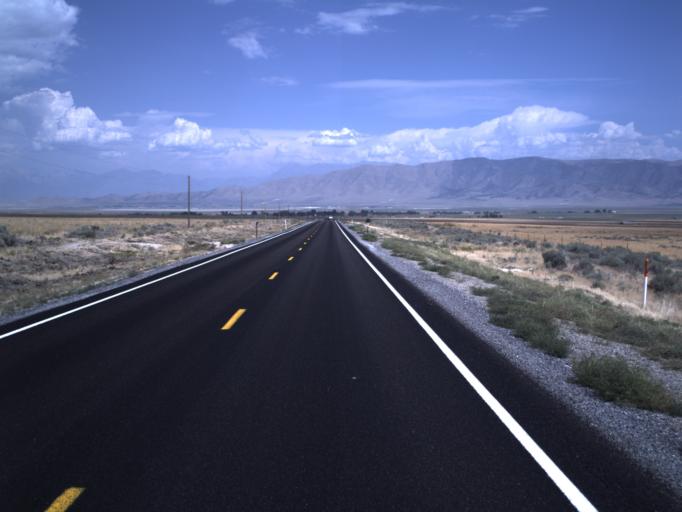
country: US
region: Utah
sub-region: Utah County
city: Eagle Mountain
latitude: 40.2454
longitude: -112.1360
